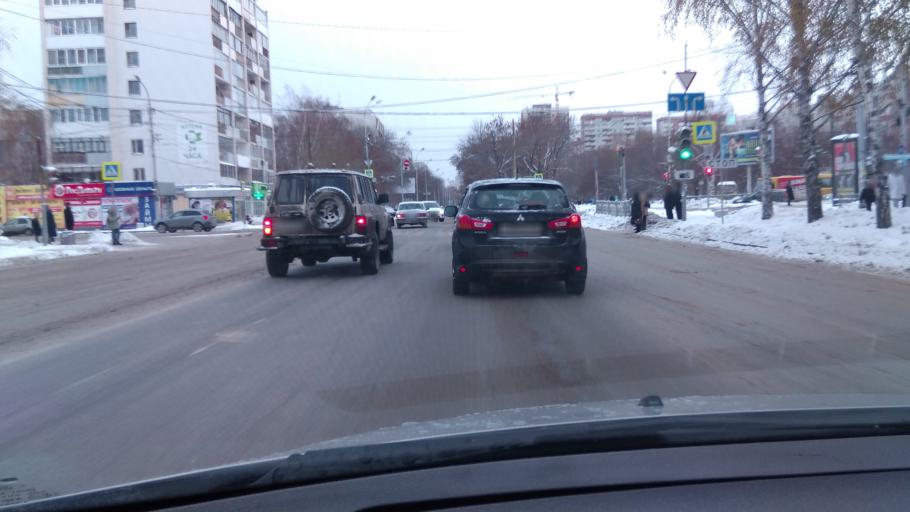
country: RU
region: Sverdlovsk
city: Sovkhoznyy
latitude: 56.8172
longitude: 60.5630
